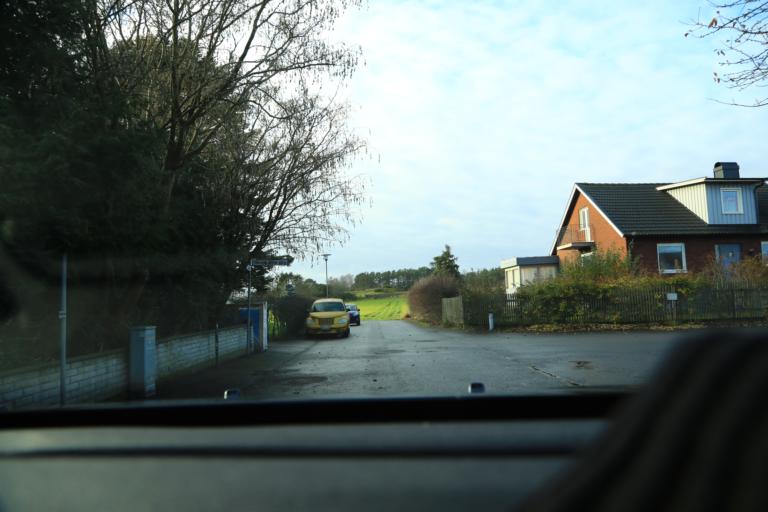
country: SE
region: Halland
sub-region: Varbergs Kommun
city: Varberg
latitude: 57.1715
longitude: 12.2247
